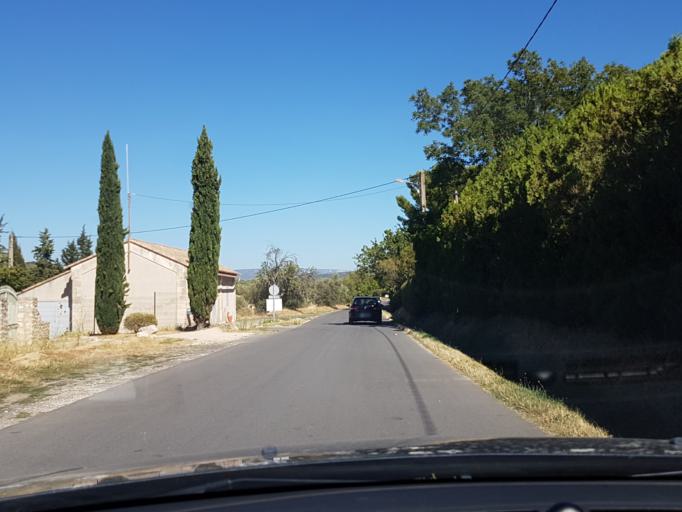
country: FR
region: Provence-Alpes-Cote d'Azur
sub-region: Departement des Bouches-du-Rhone
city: Eygalieres
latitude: 43.7607
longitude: 4.9541
